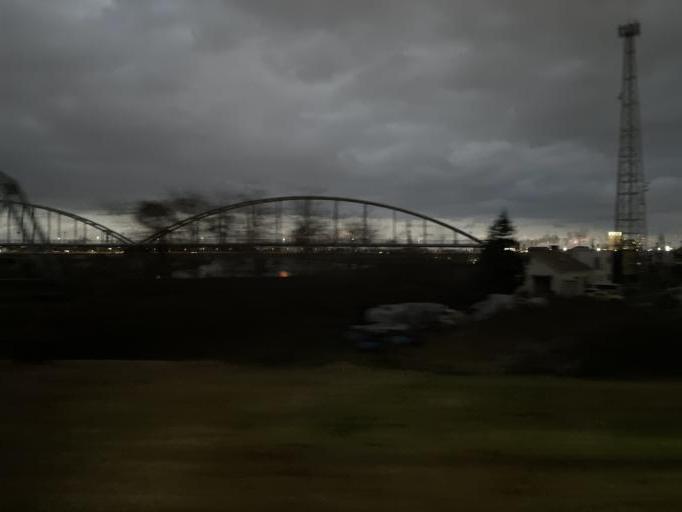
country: JP
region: Aomori
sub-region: Hachinohe Shi
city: Uchimaru
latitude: 40.5190
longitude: 141.4792
